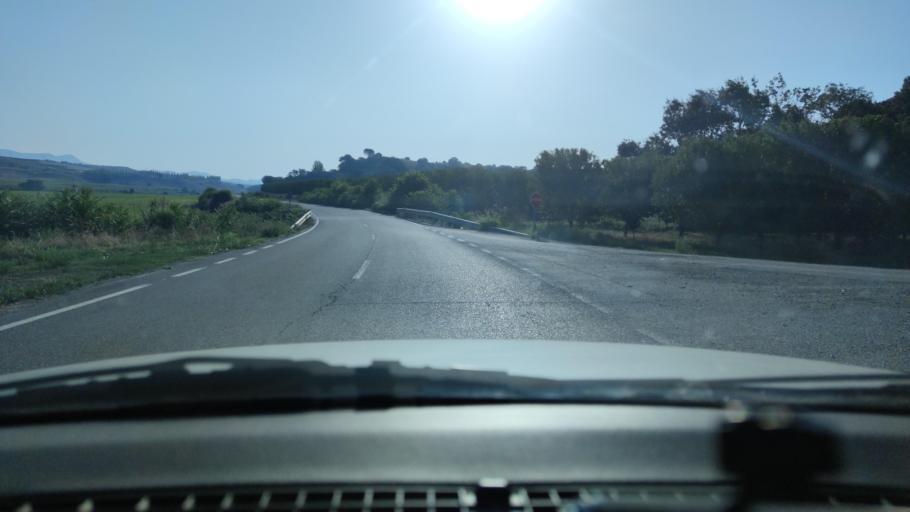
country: ES
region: Catalonia
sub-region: Provincia de Lleida
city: Balaguer
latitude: 41.7995
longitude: 0.8333
